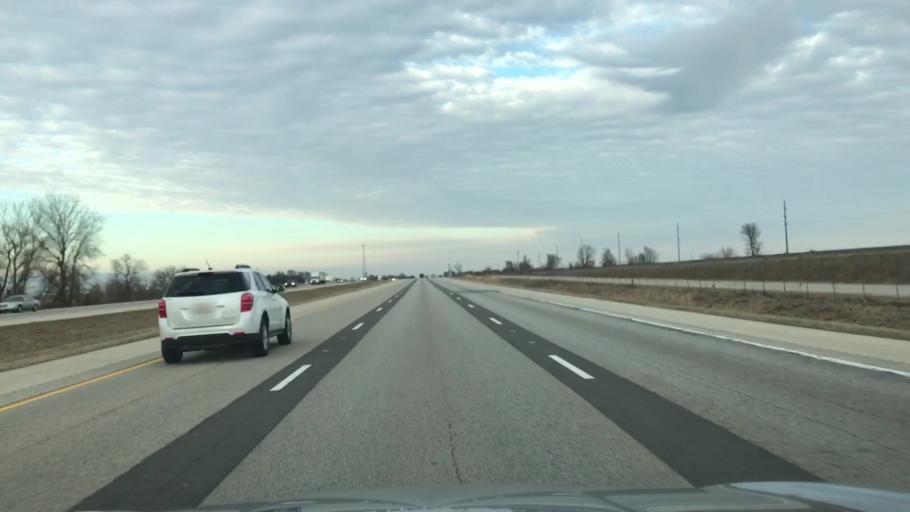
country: US
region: Illinois
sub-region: Sangamon County
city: Williamsville
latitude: 40.0463
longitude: -89.4621
